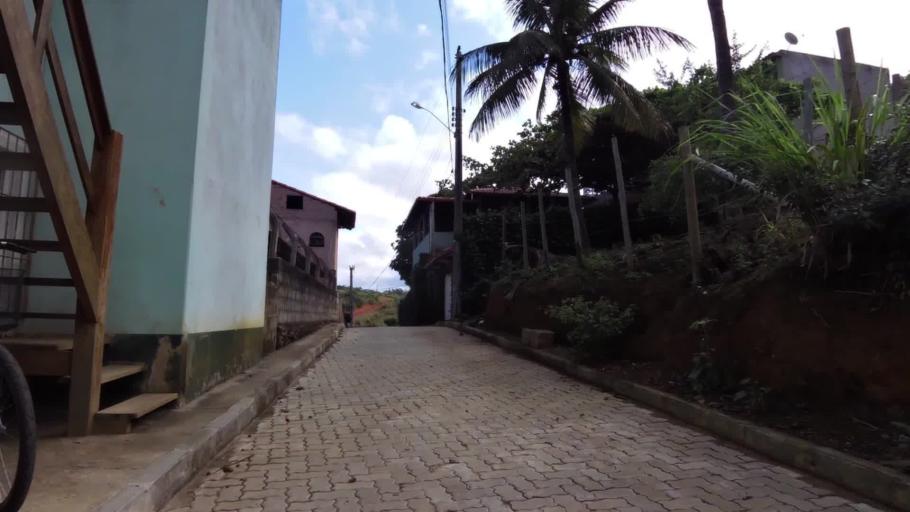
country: BR
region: Espirito Santo
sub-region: Piuma
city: Piuma
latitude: -20.8327
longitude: -40.7002
